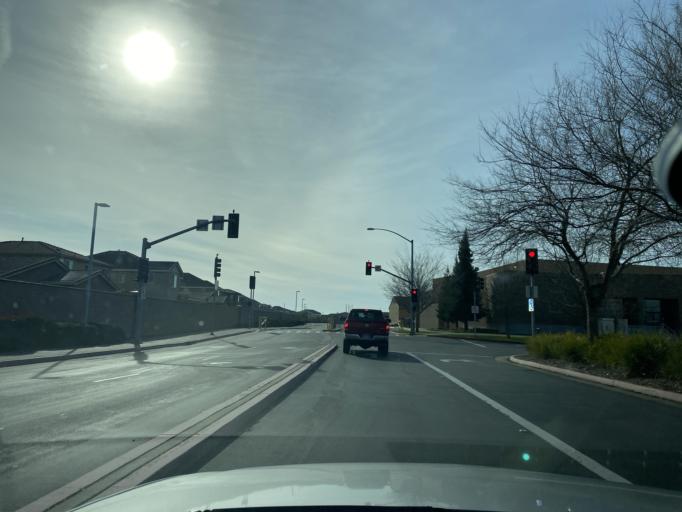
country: US
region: California
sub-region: Sacramento County
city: Elk Grove
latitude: 38.3998
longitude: -121.3947
